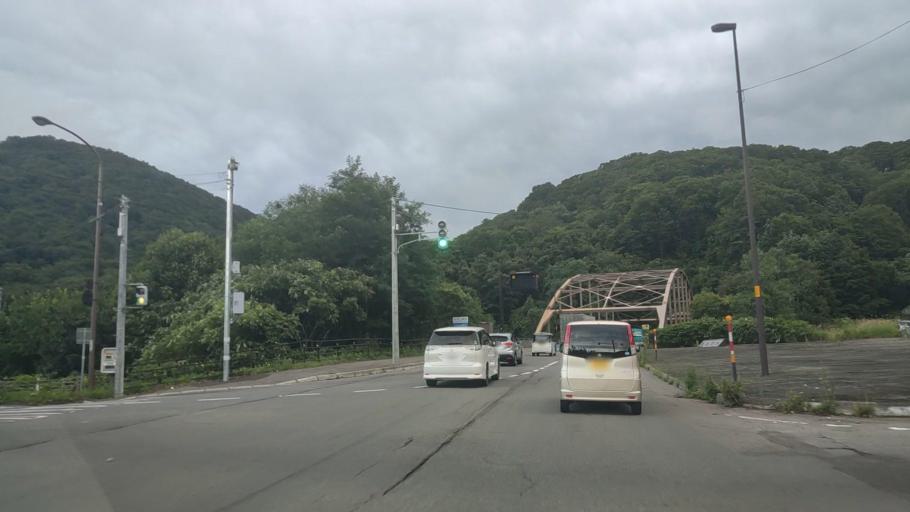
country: JP
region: Hokkaido
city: Nanae
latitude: 41.9566
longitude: 140.6504
